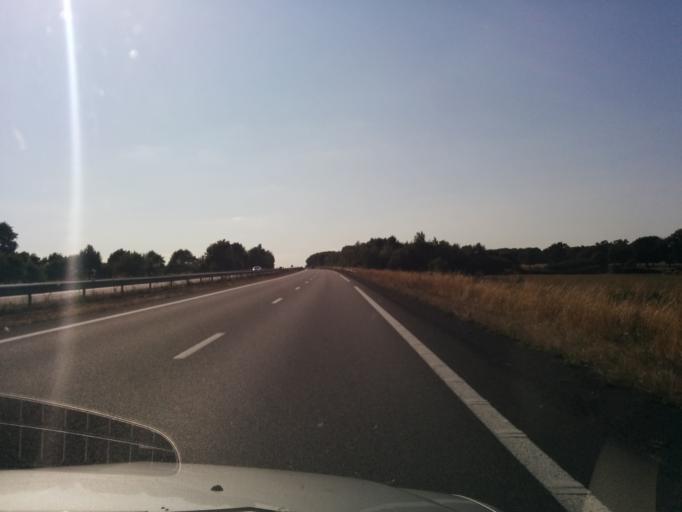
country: FR
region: Pays de la Loire
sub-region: Departement de Maine-et-Loire
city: Saint-Germain-sur-Moine
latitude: 47.1287
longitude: -1.1248
